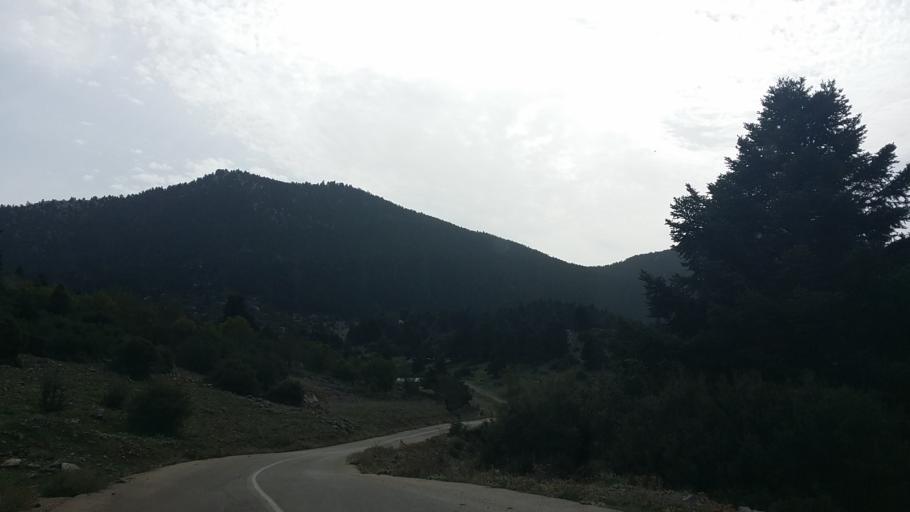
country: GR
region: Central Greece
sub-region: Nomos Voiotias
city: Livadeia
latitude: 38.3770
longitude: 22.8455
